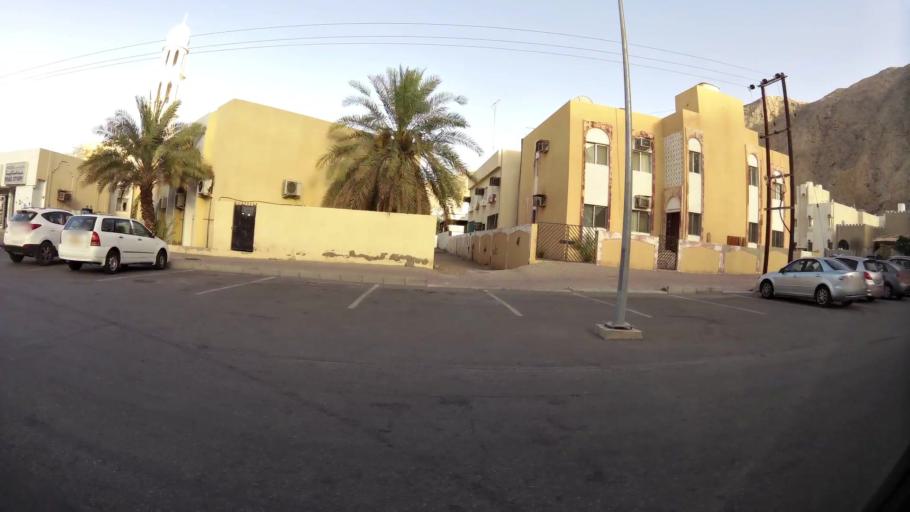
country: OM
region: Muhafazat Masqat
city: Muscat
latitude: 23.5695
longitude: 58.5693
